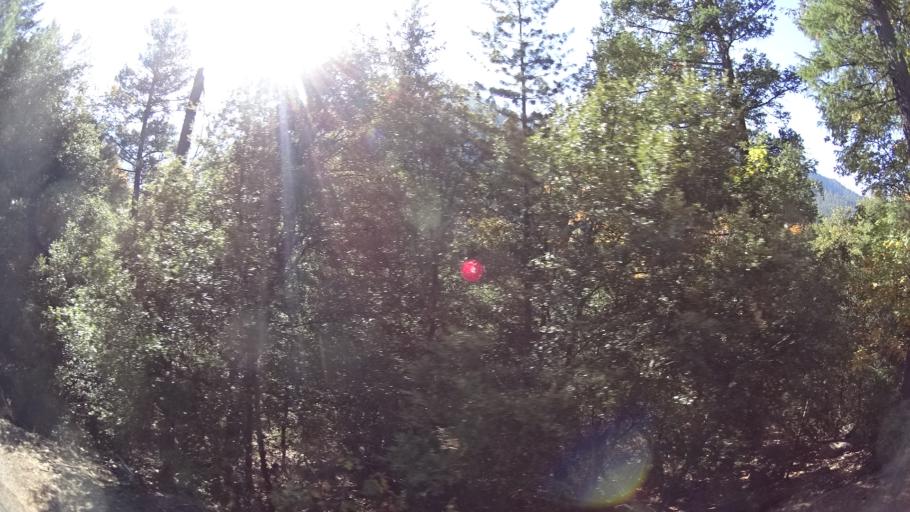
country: US
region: California
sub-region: Siskiyou County
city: Happy Camp
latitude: 41.7005
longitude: -123.0466
